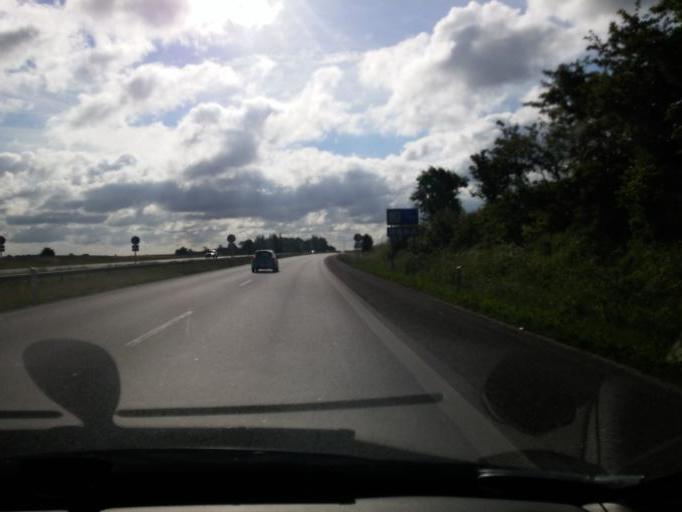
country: DK
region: Zealand
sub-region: Ringsted Kommune
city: Ringsted
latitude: 55.4558
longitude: 11.8376
